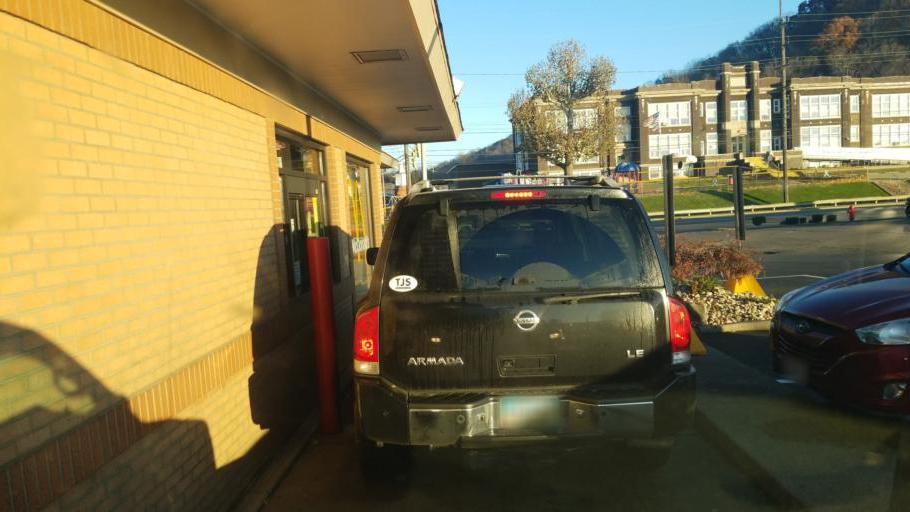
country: US
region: Kentucky
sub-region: Greenup County
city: South Shore
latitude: 38.7398
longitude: -82.9644
